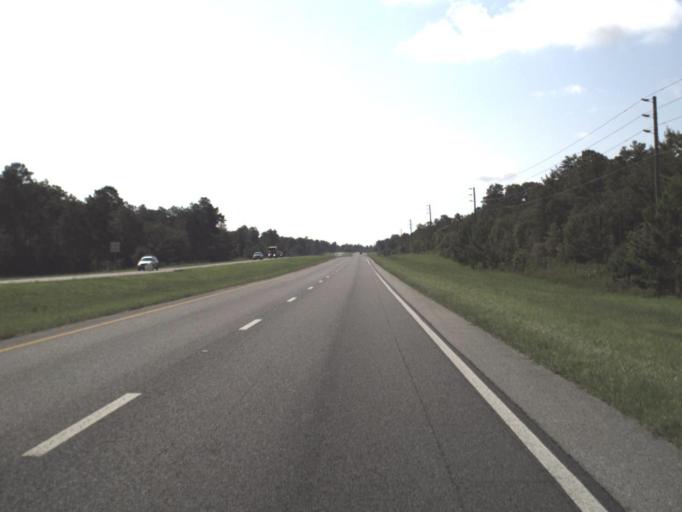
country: US
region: Florida
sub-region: Citrus County
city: Sugarmill Woods
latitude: 28.7097
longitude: -82.5298
